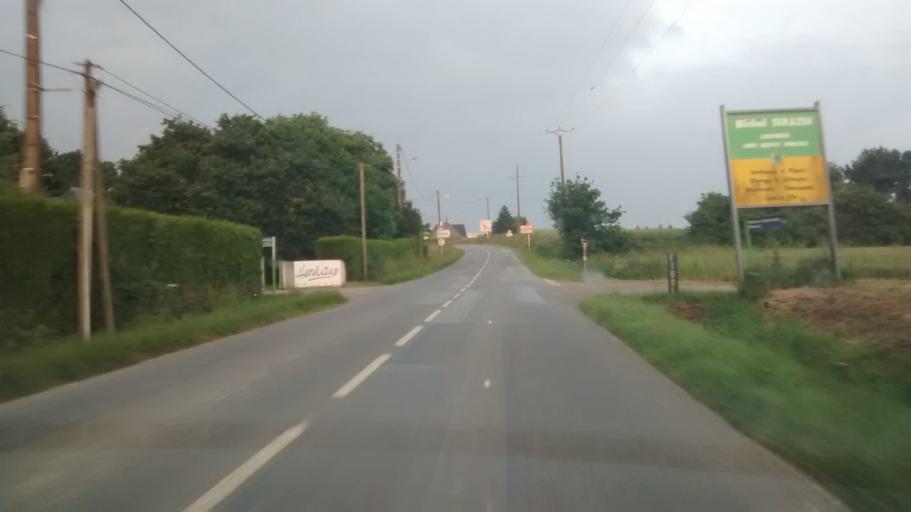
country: FR
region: Brittany
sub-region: Departement du Morbihan
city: Guer
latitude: 47.9027
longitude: -2.1263
